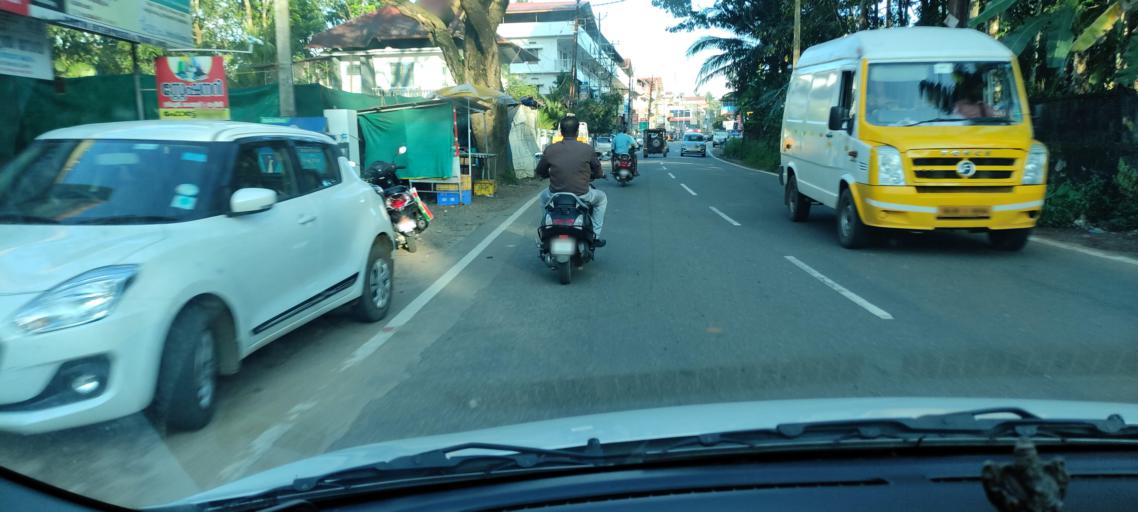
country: IN
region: Kerala
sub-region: Pattanamtitta
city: Adur
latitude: 9.1450
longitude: 76.7673
